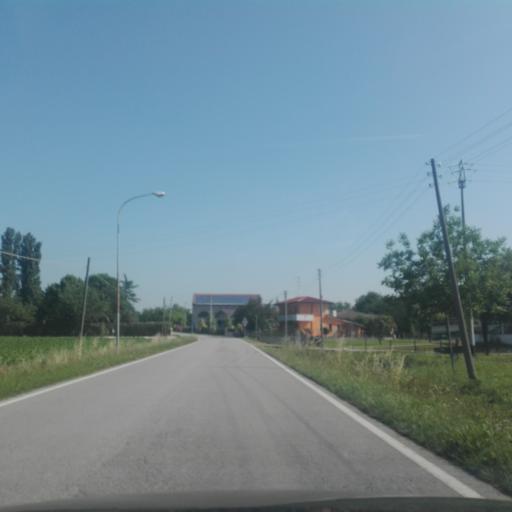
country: IT
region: Veneto
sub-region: Provincia di Rovigo
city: Gavello
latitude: 45.0321
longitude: 11.9191
